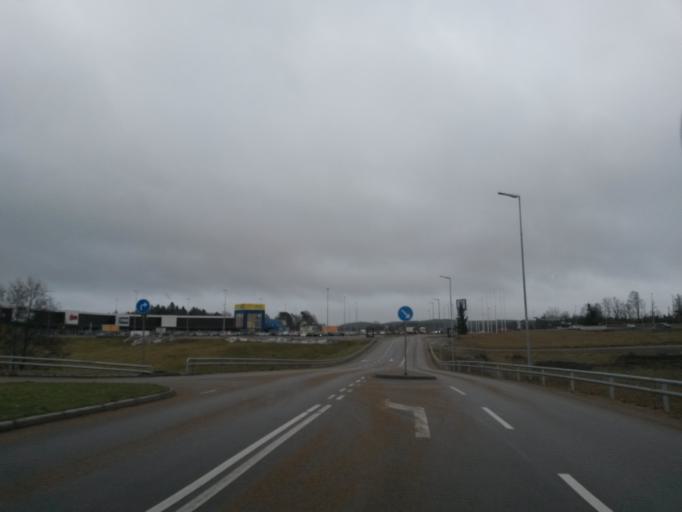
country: SE
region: Vaestra Goetaland
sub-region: Uddevalla Kommun
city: Uddevalla
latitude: 58.3542
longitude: 11.8208
